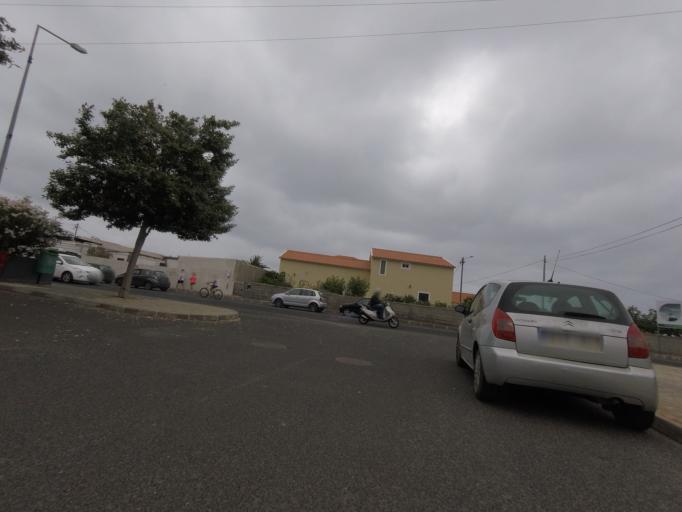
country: PT
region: Madeira
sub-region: Porto Santo
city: Vila de Porto Santo
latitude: 33.0498
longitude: -16.3515
